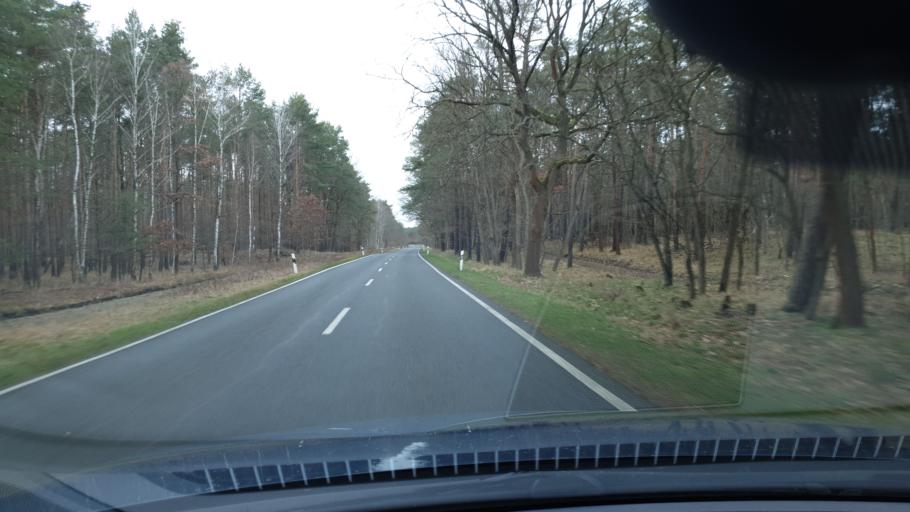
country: DE
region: Saxony-Anhalt
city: Radis
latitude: 51.7657
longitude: 12.4977
